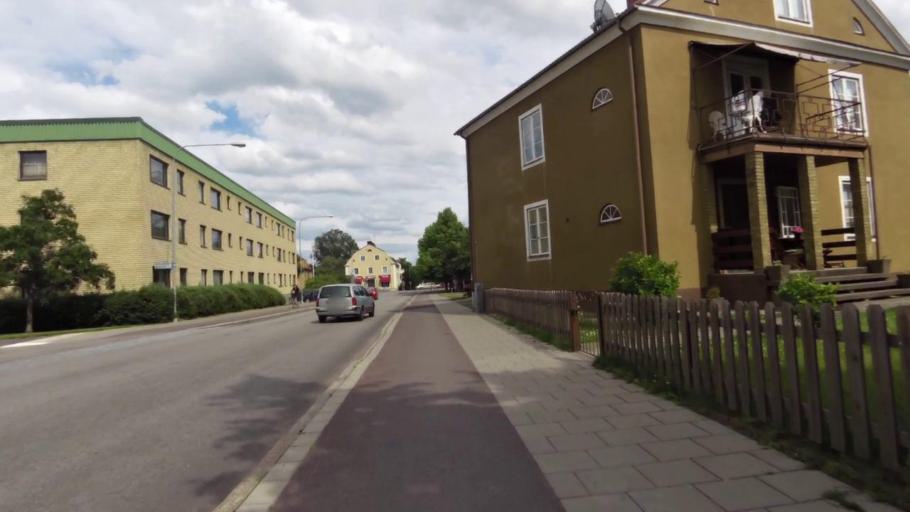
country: SE
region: OEstergoetland
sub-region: Linkopings Kommun
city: Linkoping
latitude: 58.4127
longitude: 15.6044
